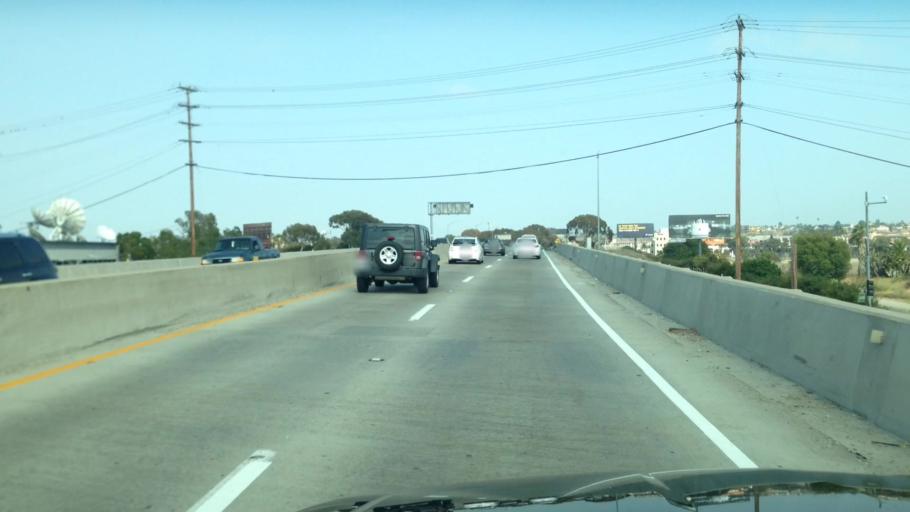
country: US
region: California
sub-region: Los Angeles County
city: Marina del Rey
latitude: 33.9817
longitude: -118.4293
